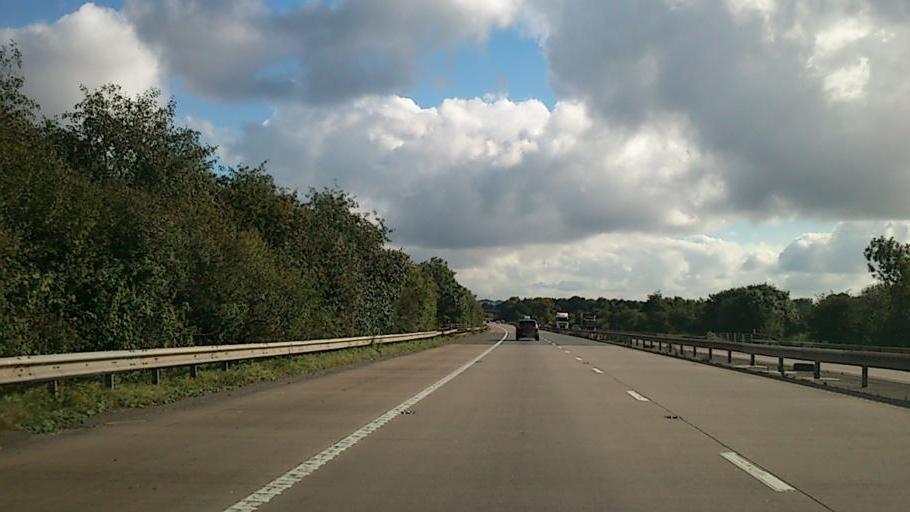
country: GB
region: England
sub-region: Staffordshire
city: Brewood
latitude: 52.6411
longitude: -2.1605
